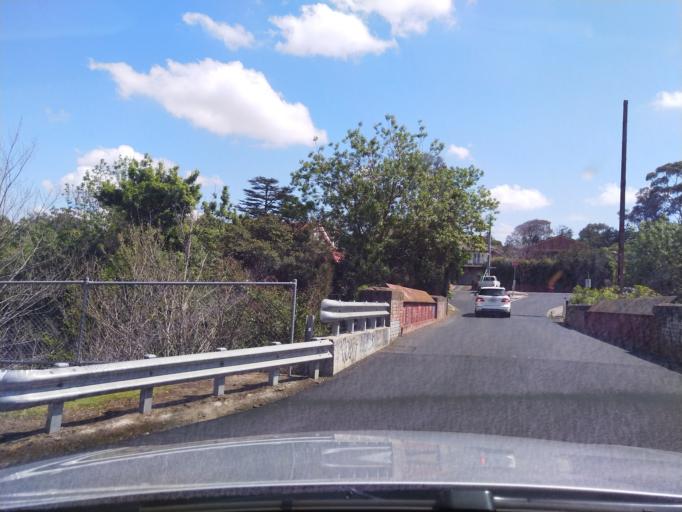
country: AU
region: Victoria
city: Rosanna
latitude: -37.7607
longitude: 145.0571
